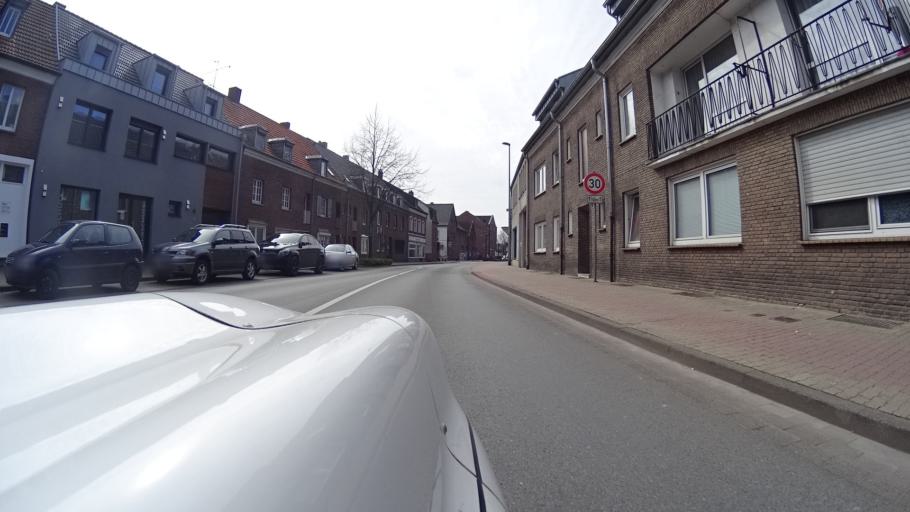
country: DE
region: North Rhine-Westphalia
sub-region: Regierungsbezirk Dusseldorf
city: Kevelaer
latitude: 51.5861
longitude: 6.2421
